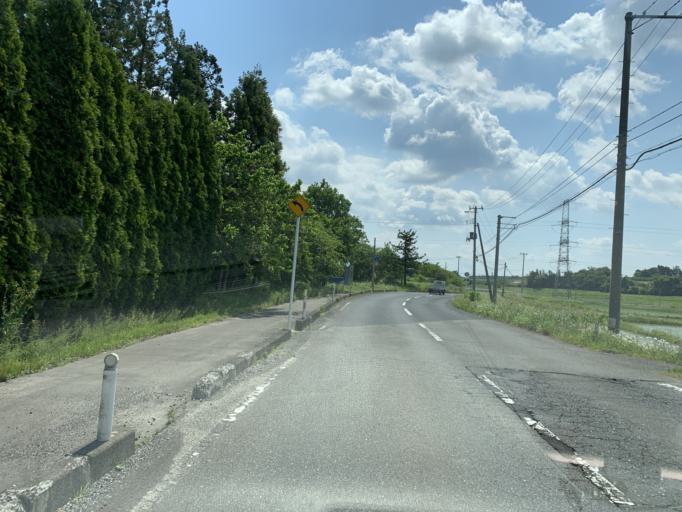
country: JP
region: Miyagi
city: Furukawa
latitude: 38.6902
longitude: 140.9401
